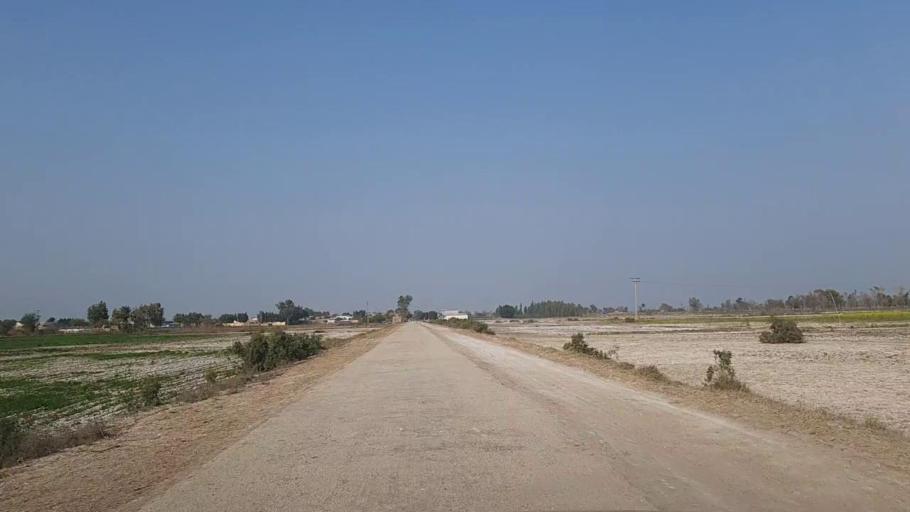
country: PK
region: Sindh
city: Daur
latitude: 26.4223
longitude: 68.4089
